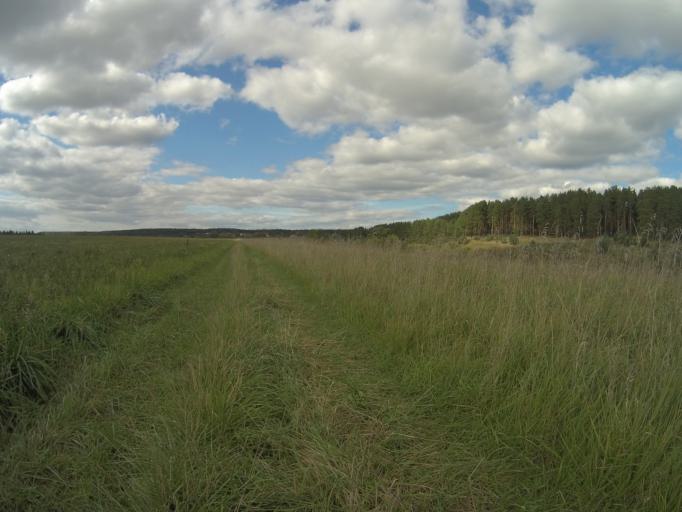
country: RU
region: Vladimir
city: Orgtrud
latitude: 56.3188
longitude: 40.6805
